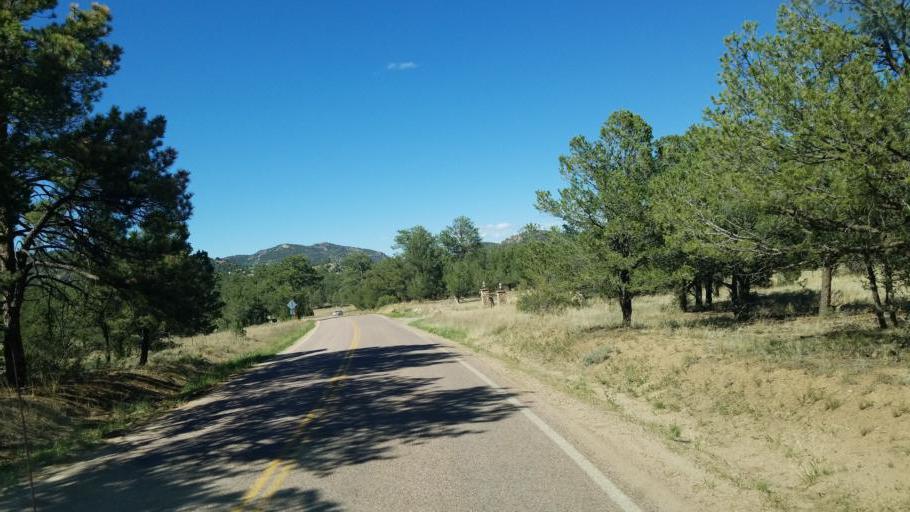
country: US
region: Colorado
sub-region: Custer County
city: Westcliffe
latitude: 38.3581
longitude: -105.4727
